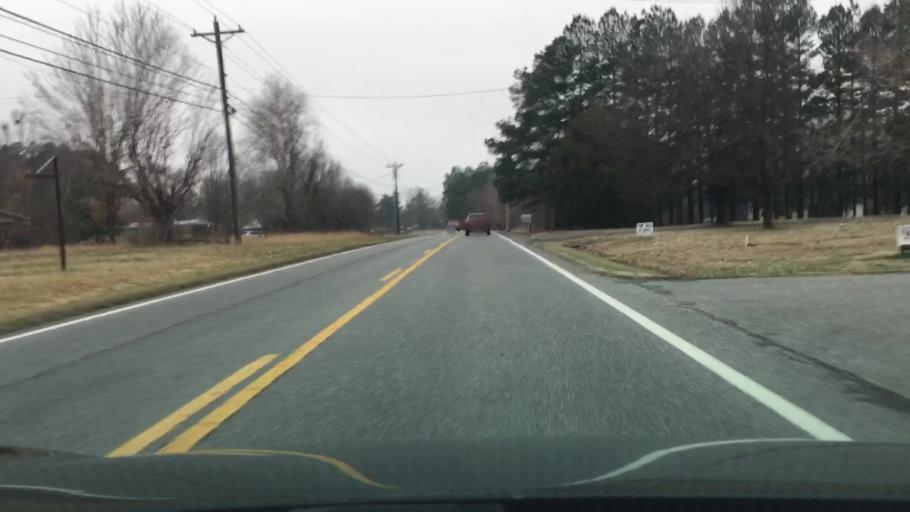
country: US
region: Kentucky
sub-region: Marshall County
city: Calvert City
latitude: 36.9712
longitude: -88.4139
